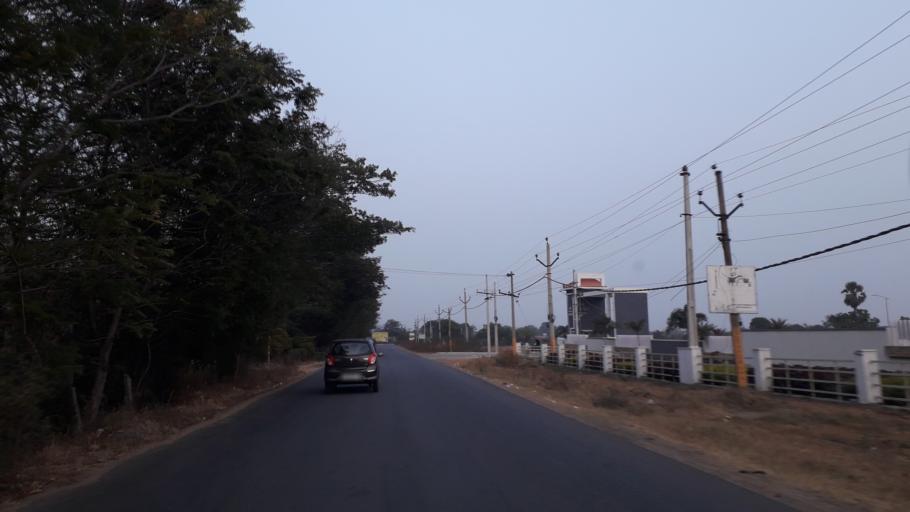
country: IN
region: Telangana
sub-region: Medak
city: Patancheru
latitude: 17.5069
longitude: 78.2059
